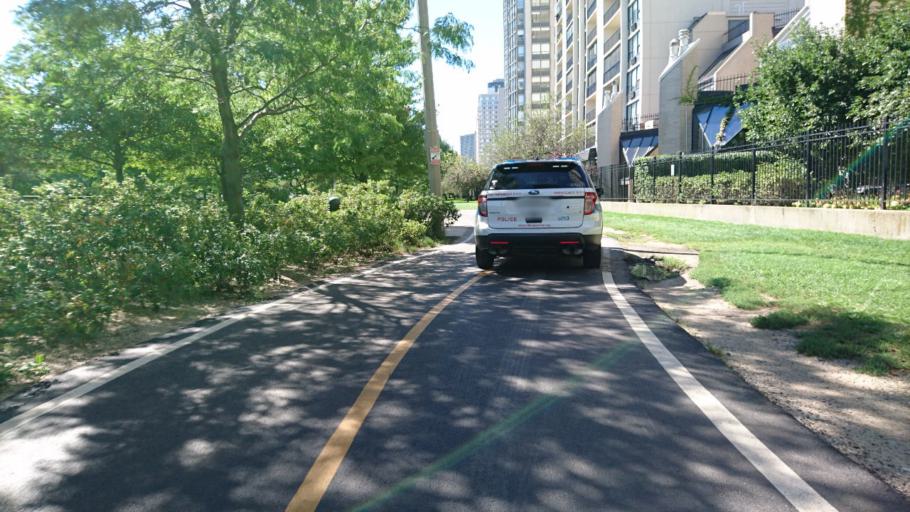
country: US
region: Illinois
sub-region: Cook County
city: Evanston
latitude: 41.9873
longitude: -87.6541
